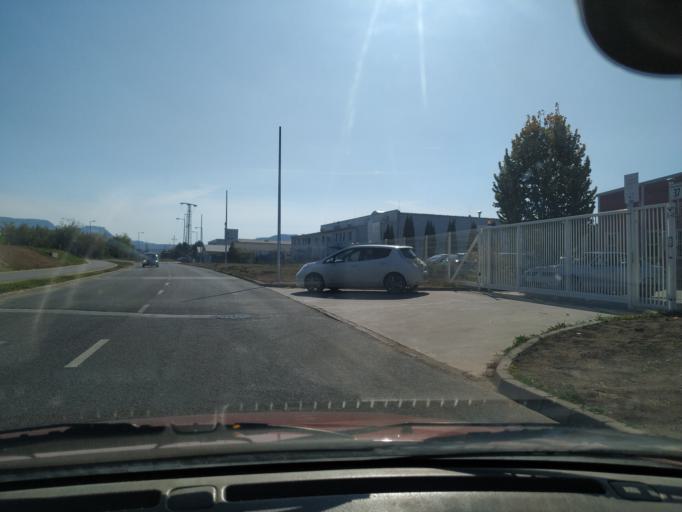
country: HU
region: Komarom-Esztergom
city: Esztergom
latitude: 47.7752
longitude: 18.7500
